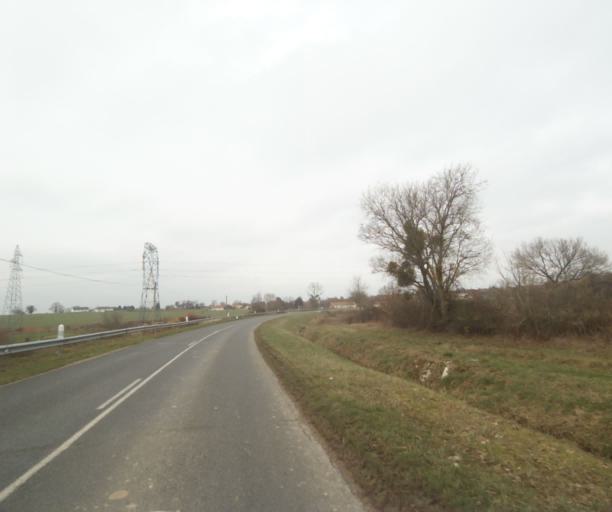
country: FR
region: Champagne-Ardenne
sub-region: Departement de la Marne
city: Pargny-sur-Saulx
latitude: 48.7430
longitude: 4.8495
